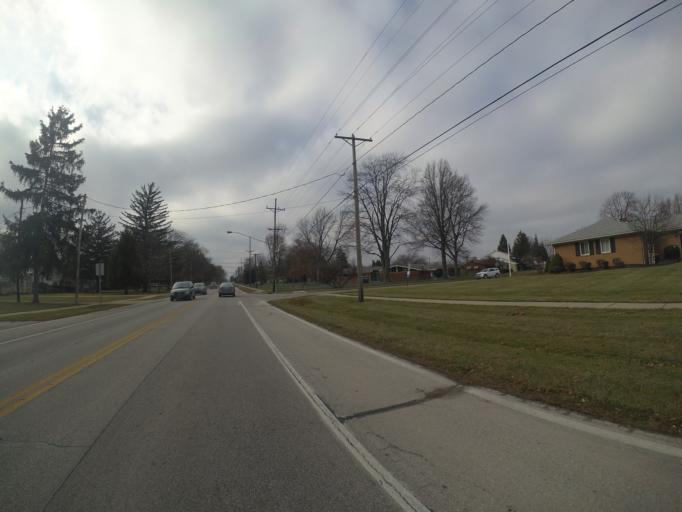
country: US
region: Ohio
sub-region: Lucas County
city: Oregon
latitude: 41.6442
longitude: -83.4775
